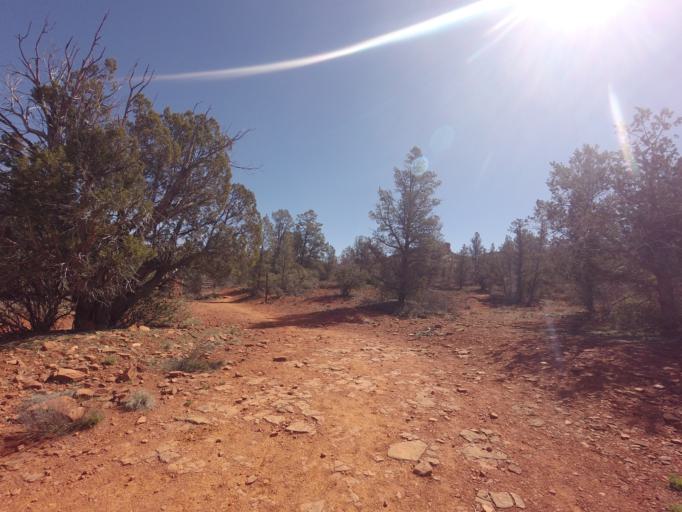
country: US
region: Arizona
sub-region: Yavapai County
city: West Sedona
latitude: 34.8082
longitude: -111.8204
